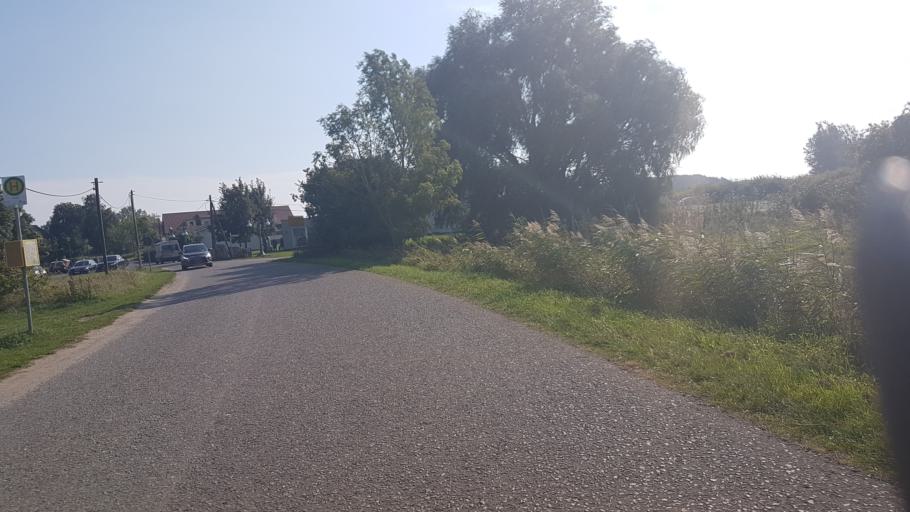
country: DE
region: Mecklenburg-Vorpommern
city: Putbus
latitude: 54.3283
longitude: 13.4629
